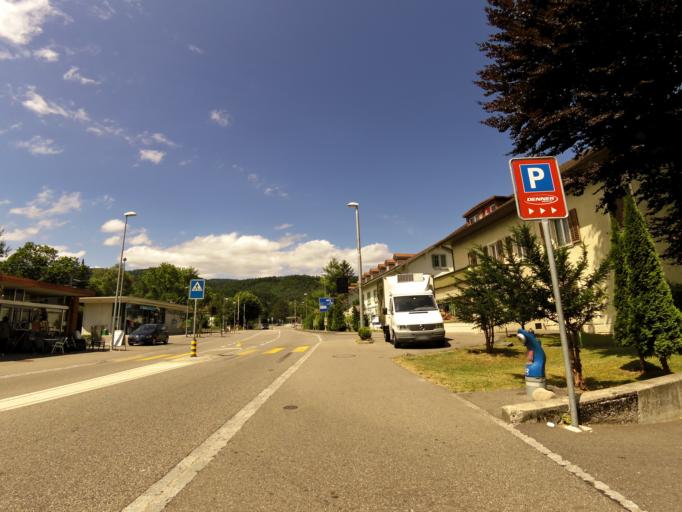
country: CH
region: Solothurn
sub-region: Bezirk Thal
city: Balsthal
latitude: 47.3080
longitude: 7.6888
